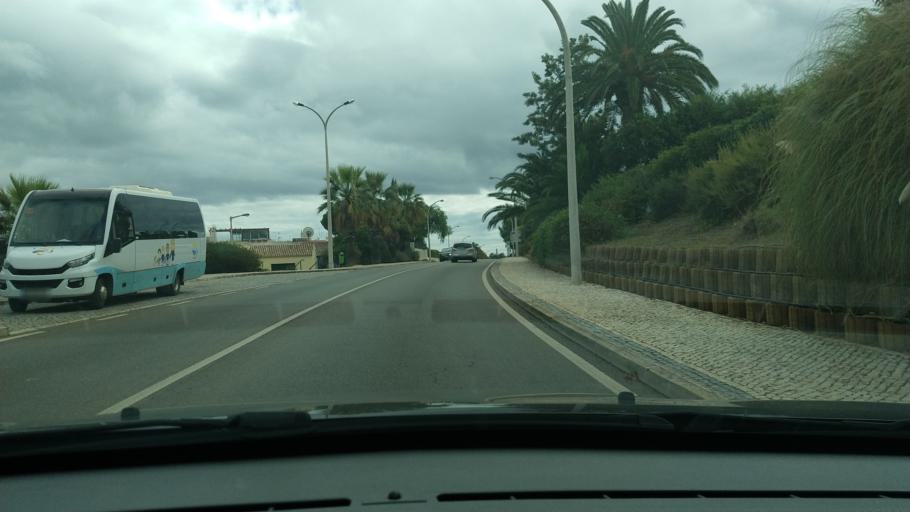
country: PT
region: Faro
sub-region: Lagos
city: Lagos
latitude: 37.0994
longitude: -8.6798
